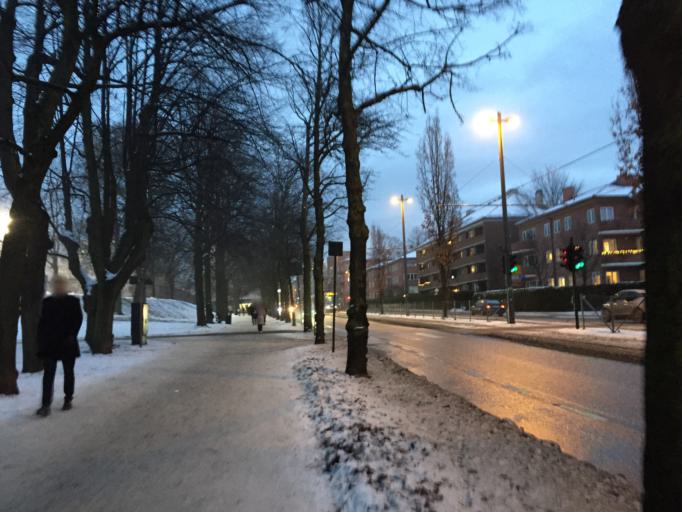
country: NO
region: Oslo
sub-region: Oslo
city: Sjolyststranda
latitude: 59.9258
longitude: 10.7101
